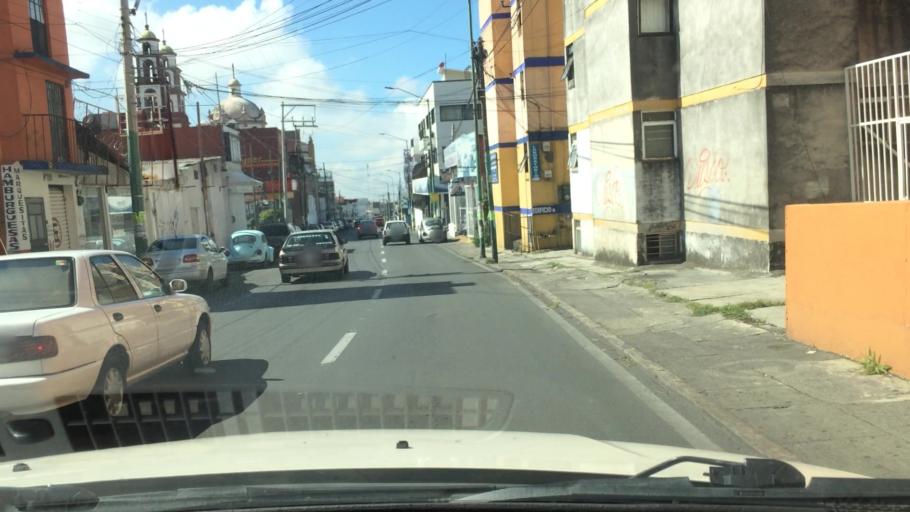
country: MX
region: Morelos
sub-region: Cuernavaca
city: Cuernavaca
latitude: 18.9395
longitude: -99.2414
